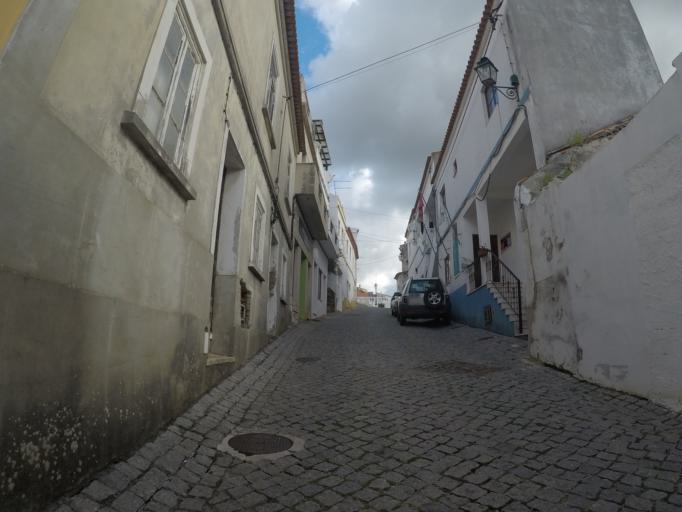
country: PT
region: Faro
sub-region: Aljezur
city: Aljezur
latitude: 37.3184
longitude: -8.8033
